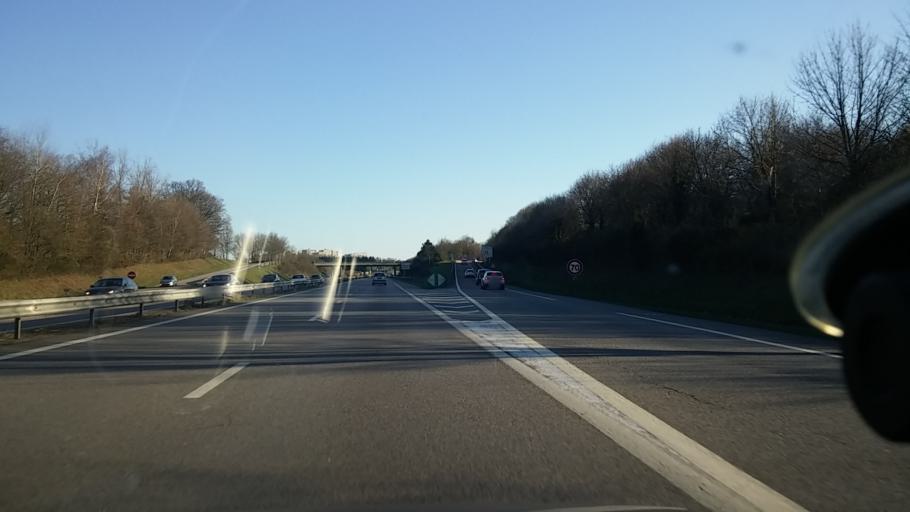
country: FR
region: Limousin
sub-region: Departement de la Haute-Vienne
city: Rilhac-Rancon
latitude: 45.8970
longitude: 1.2922
